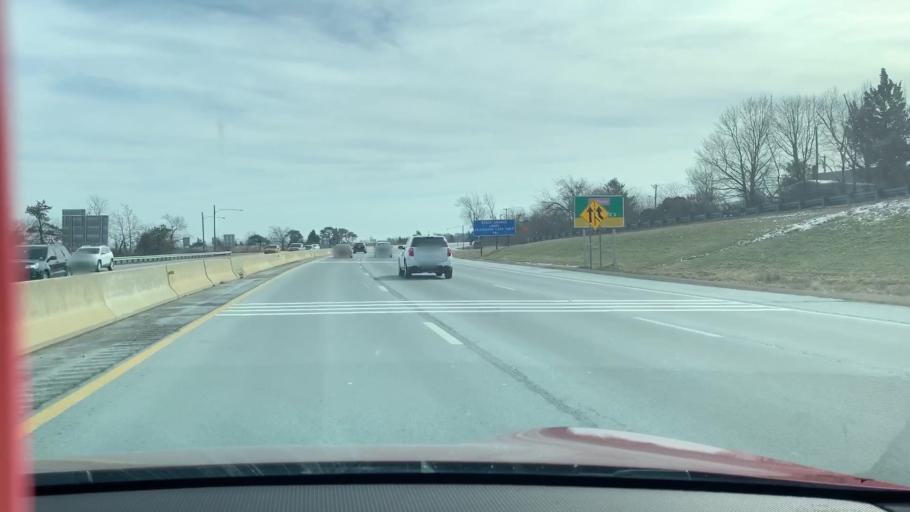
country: US
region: New Jersey
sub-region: Atlantic County
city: Pleasantville
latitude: 39.3966
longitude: -74.5141
